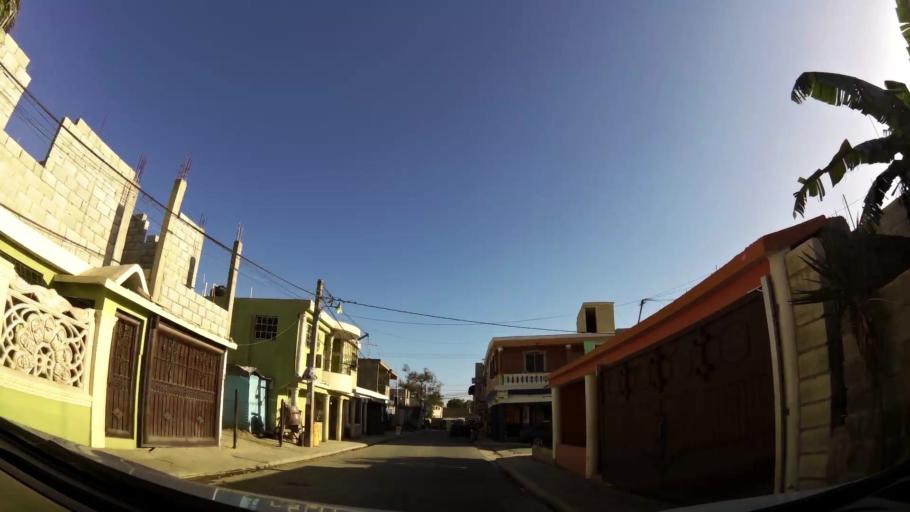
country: DO
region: Santo Domingo
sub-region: Santo Domingo
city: Santo Domingo Este
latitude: 18.4816
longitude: -69.8167
